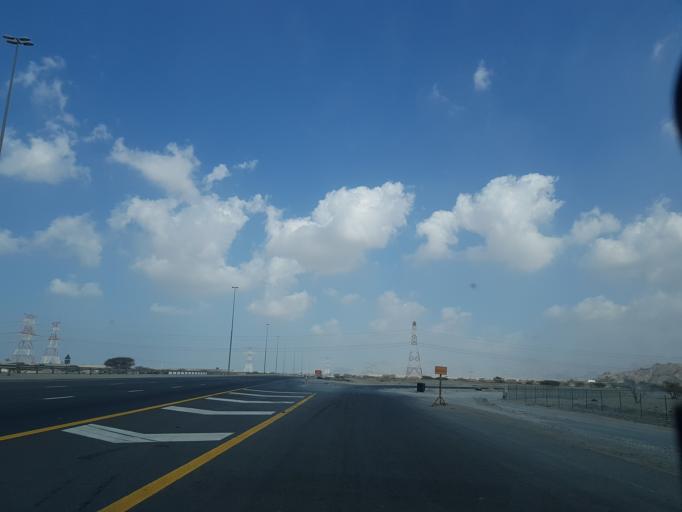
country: AE
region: Ra's al Khaymah
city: Ras al-Khaimah
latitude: 25.7446
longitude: 56.0164
